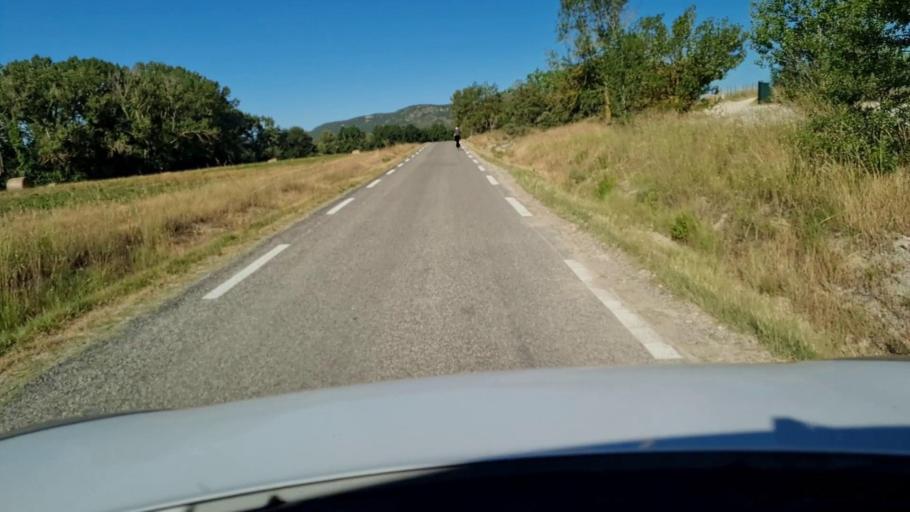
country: FR
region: Languedoc-Roussillon
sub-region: Departement du Gard
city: Sommieres
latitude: 43.8329
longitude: 4.0520
